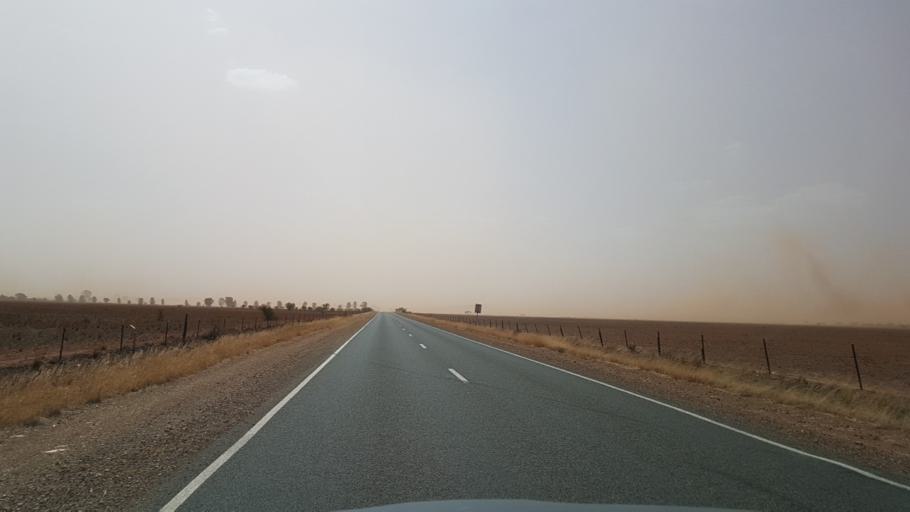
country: AU
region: South Australia
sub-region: Peterborough
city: Peterborough
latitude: -33.1272
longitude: 138.9300
